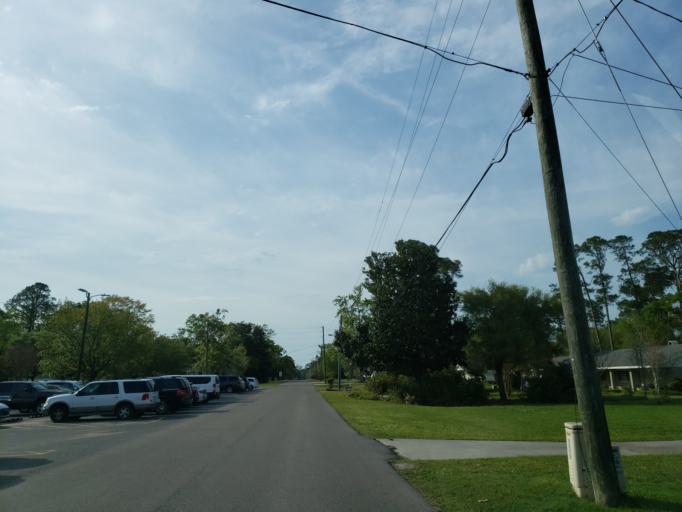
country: US
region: Mississippi
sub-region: Harrison County
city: West Gulfport
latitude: 30.4136
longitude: -89.0485
